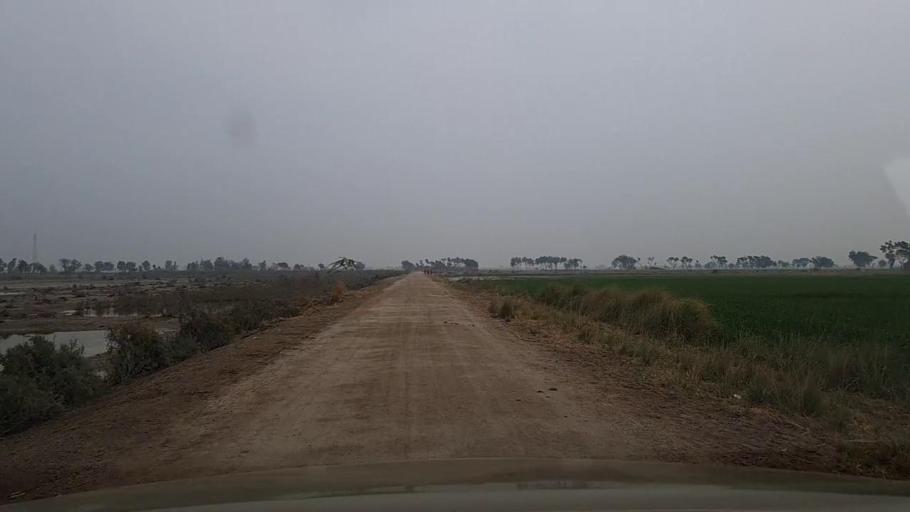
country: PK
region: Sindh
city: Sanghar
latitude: 26.1190
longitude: 68.9180
